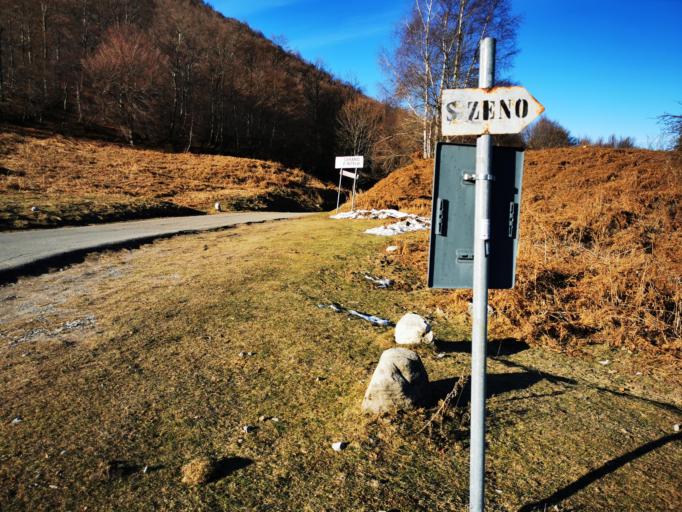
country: IT
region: Lombardy
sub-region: Provincia di Como
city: Casasco Intelvi
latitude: 45.9222
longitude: 9.0721
